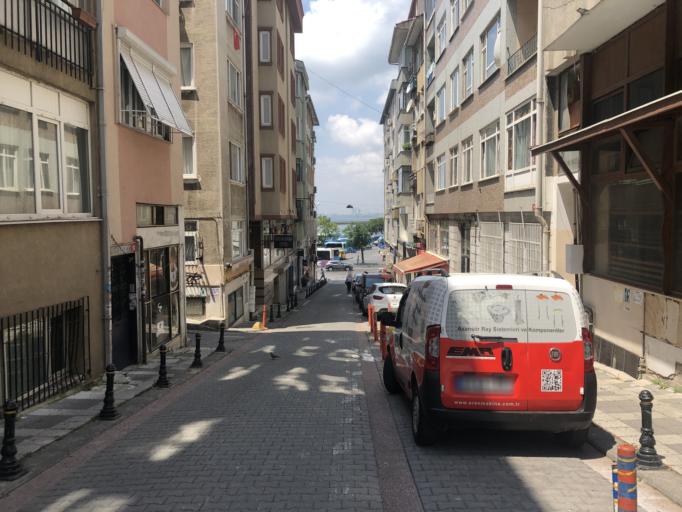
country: TR
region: Istanbul
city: UEskuedar
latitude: 40.9956
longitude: 29.0255
